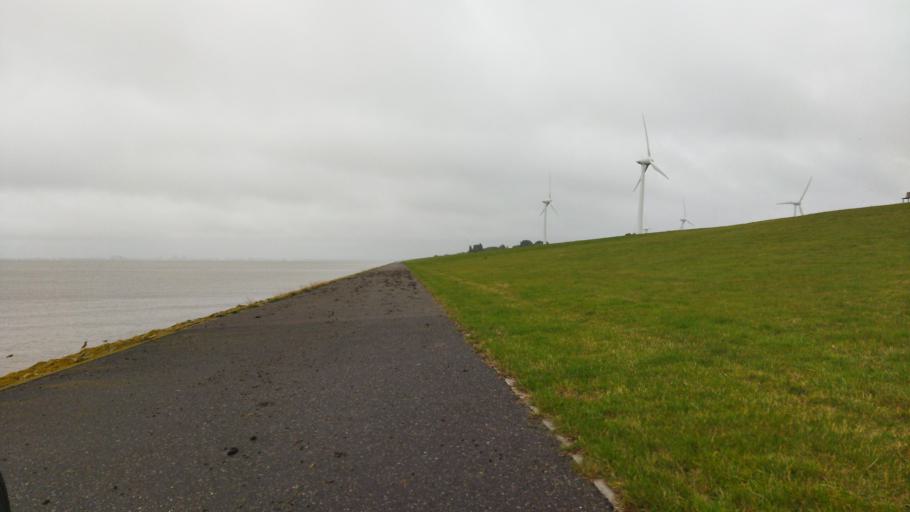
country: DE
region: Lower Saxony
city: Emden
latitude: 53.3349
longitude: 7.0925
